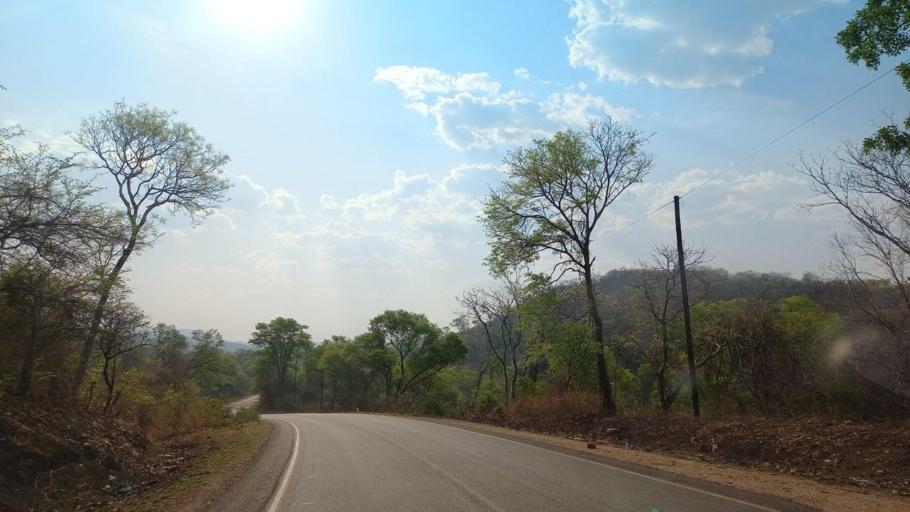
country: ZM
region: Lusaka
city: Luangwa
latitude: -14.9820
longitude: 30.1795
